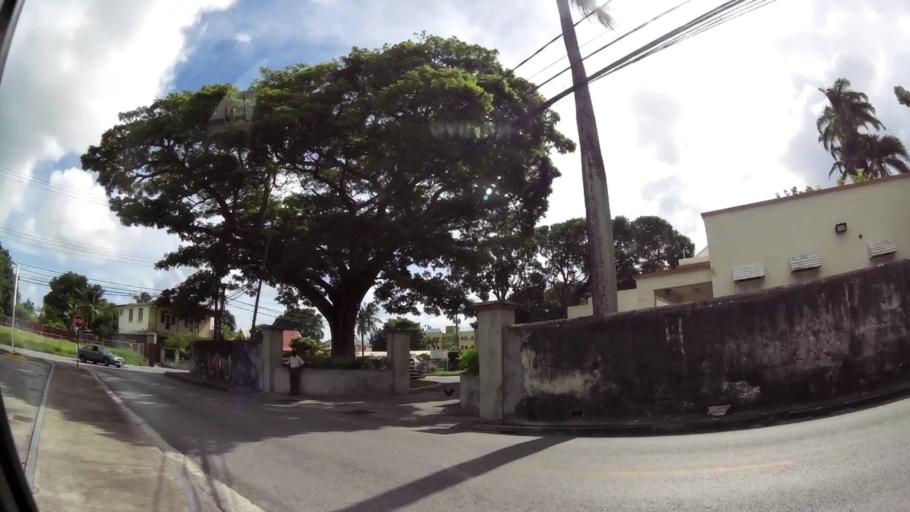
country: BB
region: Saint Michael
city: Bridgetown
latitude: 13.1080
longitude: -59.6126
